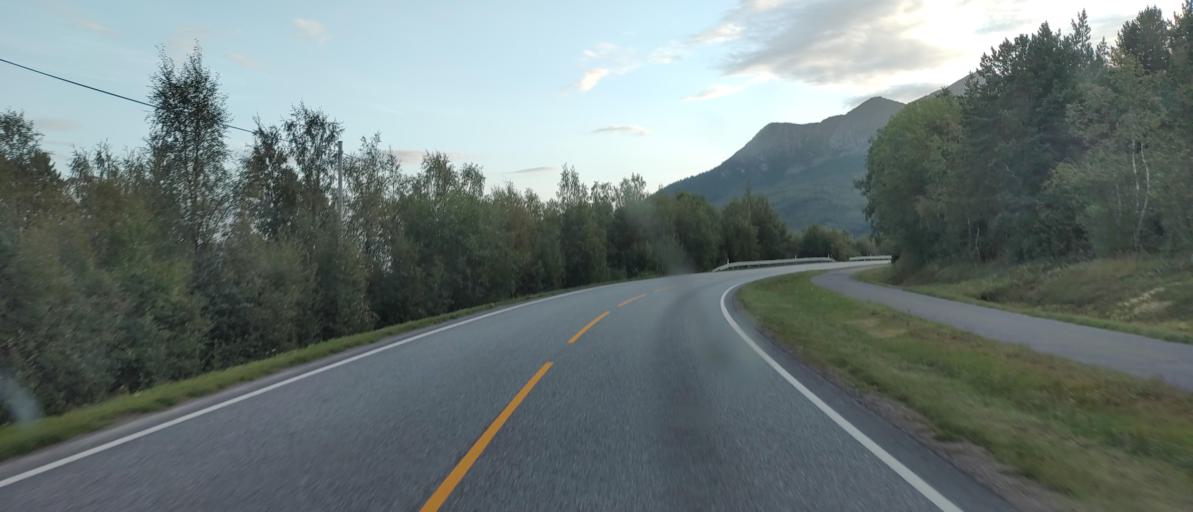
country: NO
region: Nordland
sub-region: Lodingen
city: Lodingen
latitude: 68.1944
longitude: 16.0568
